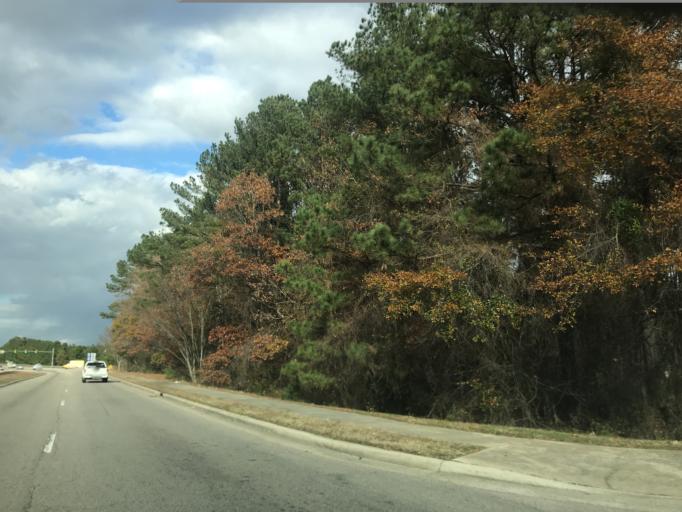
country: US
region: North Carolina
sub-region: Wake County
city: Raleigh
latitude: 35.7737
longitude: -78.5603
